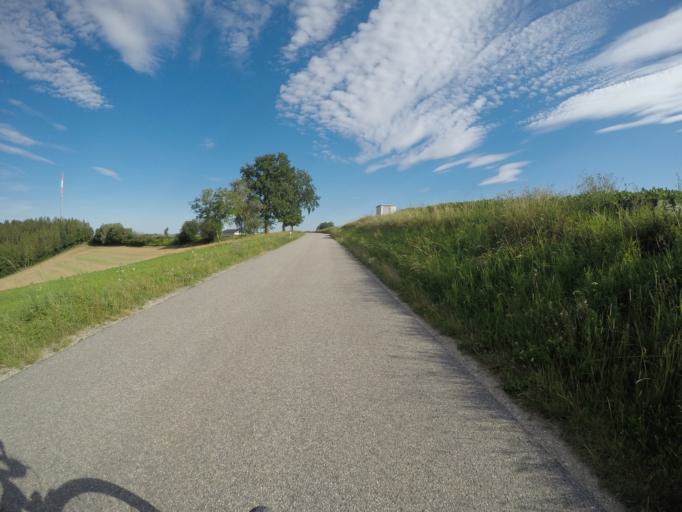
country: DE
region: Bavaria
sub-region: Lower Bavaria
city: Tiefenbach
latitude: 48.5112
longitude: 12.1268
